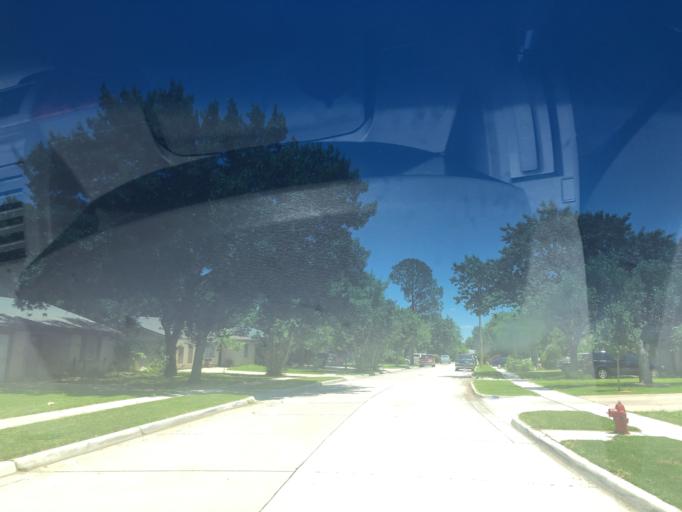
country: US
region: Texas
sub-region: Dallas County
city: Grand Prairie
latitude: 32.7160
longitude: -97.0056
